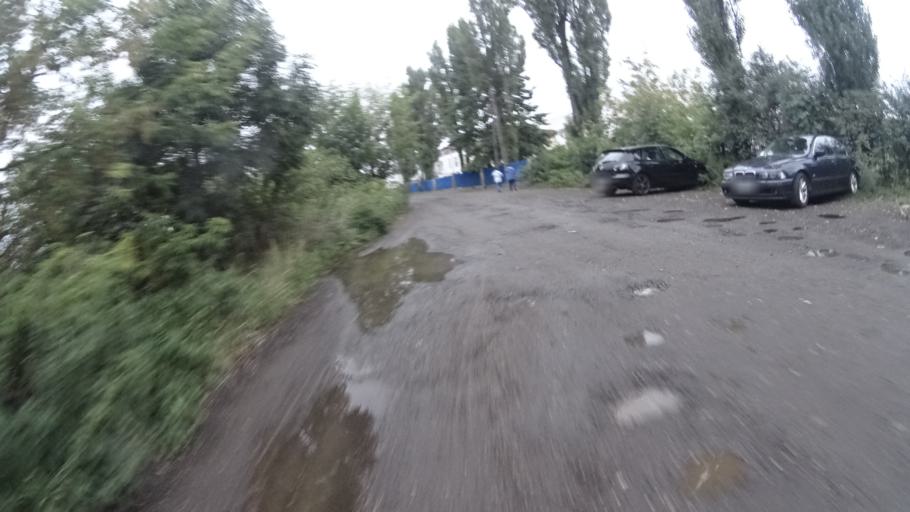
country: PL
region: Masovian Voivodeship
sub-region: Powiat warszawski zachodni
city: Babice
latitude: 52.2250
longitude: 20.8637
